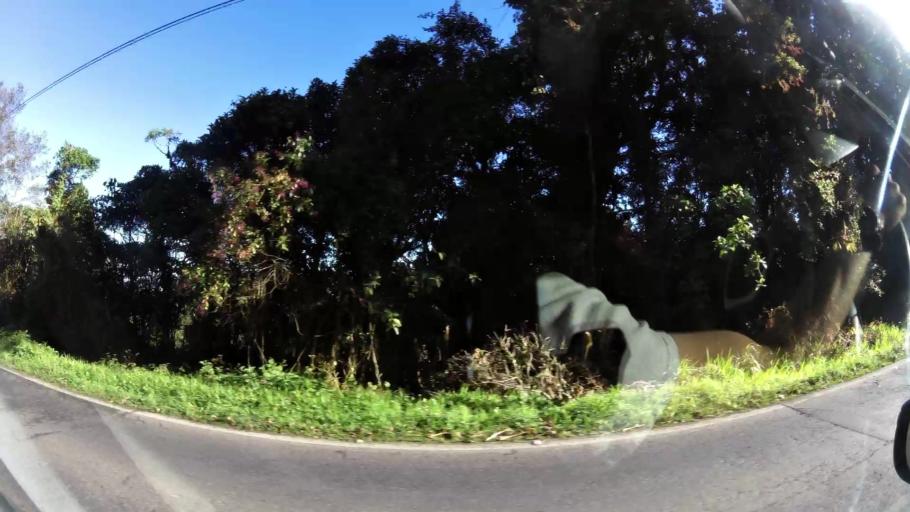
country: CR
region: San Jose
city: San Marcos
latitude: 9.6954
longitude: -83.9270
